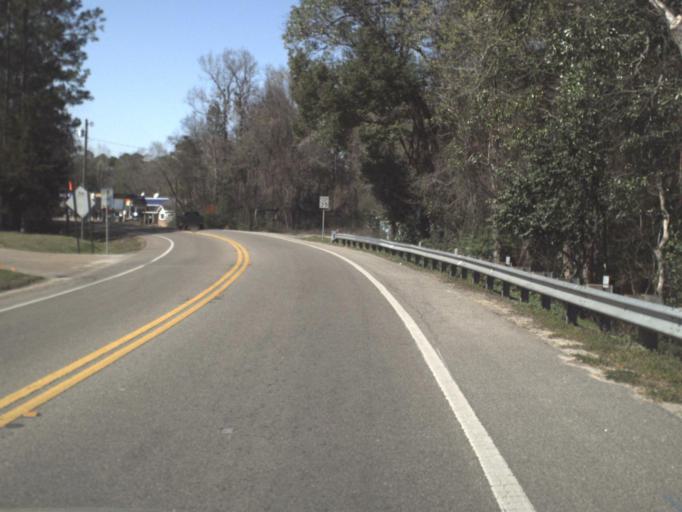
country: US
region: Florida
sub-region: Calhoun County
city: Blountstown
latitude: 30.4508
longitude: -85.0461
